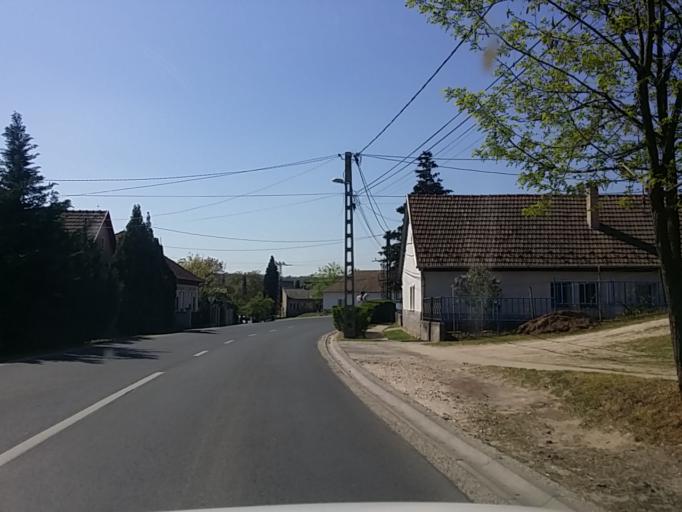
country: HU
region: Pest
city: Mogyorod
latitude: 47.5977
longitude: 19.2379
